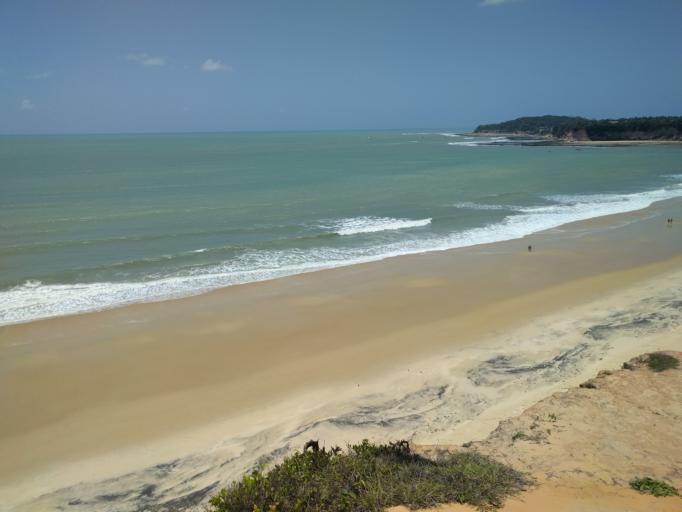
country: BR
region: Rio Grande do Norte
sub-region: Ares
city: Ares
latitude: -6.2232
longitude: -35.0661
